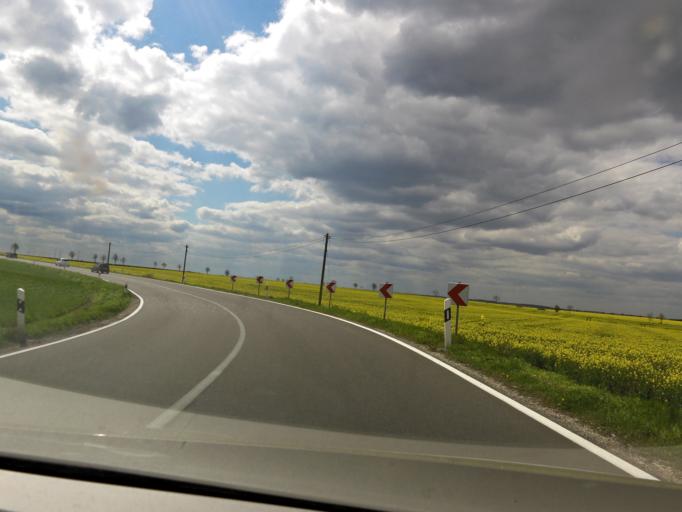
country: DE
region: Saxony-Anhalt
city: Leissling
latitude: 51.1748
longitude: 11.9259
